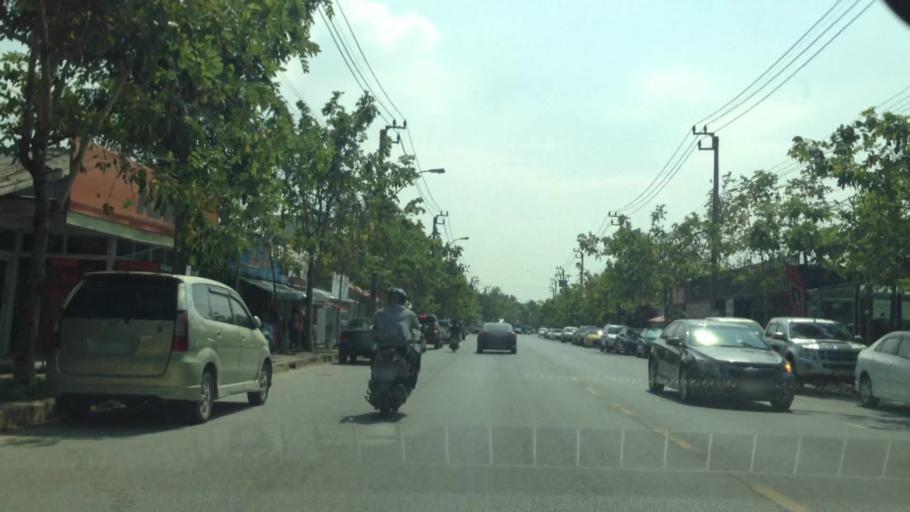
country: TH
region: Bangkok
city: Bang Khen
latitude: 13.8886
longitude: 100.6429
